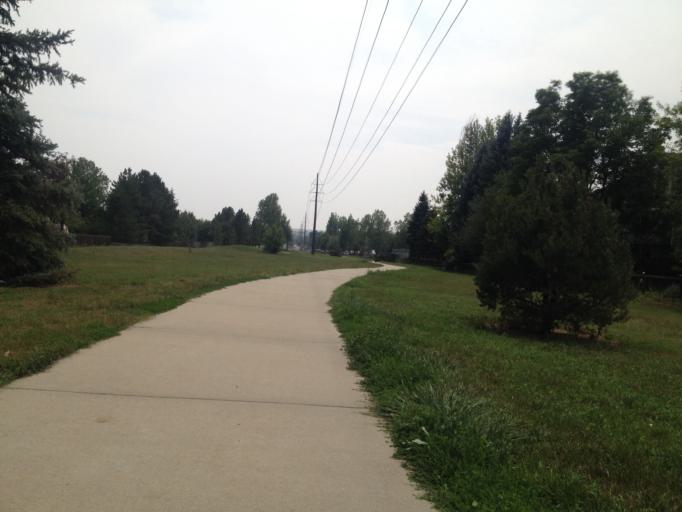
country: US
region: Colorado
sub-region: Boulder County
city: Superior
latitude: 39.9714
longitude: -105.1562
